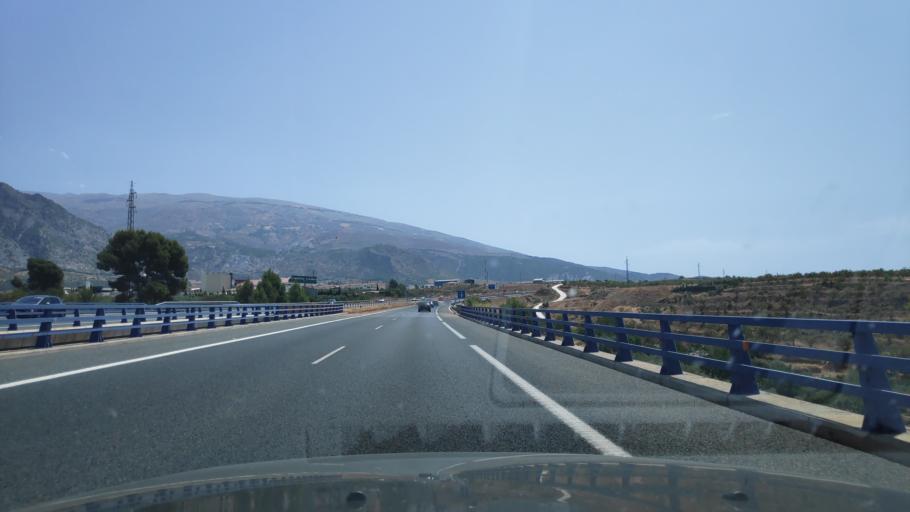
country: ES
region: Andalusia
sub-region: Provincia de Granada
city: Durcal
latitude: 36.9800
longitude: -3.5701
